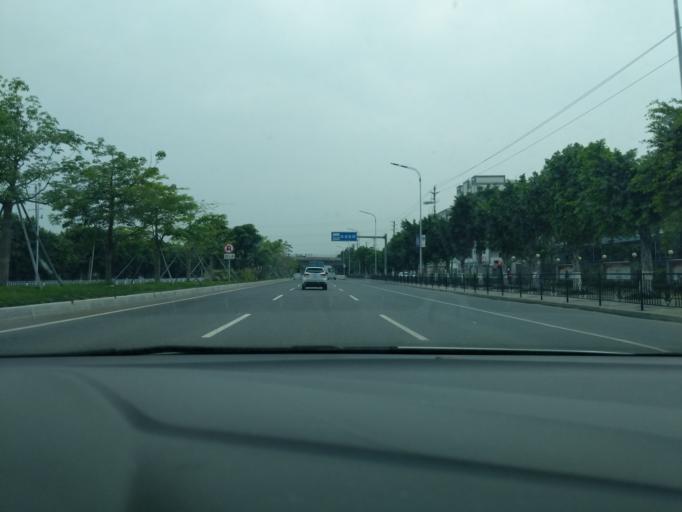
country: CN
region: Guangdong
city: Huangge
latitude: 22.8598
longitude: 113.4858
